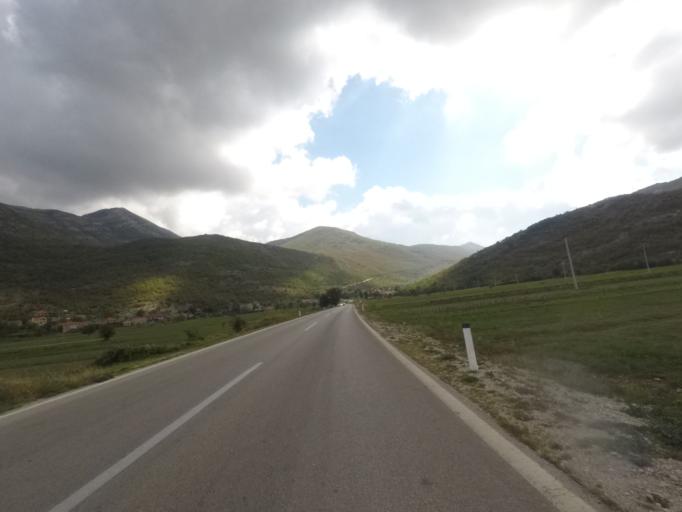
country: BA
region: Republika Srpska
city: Trebinje
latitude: 42.6082
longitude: 18.4202
